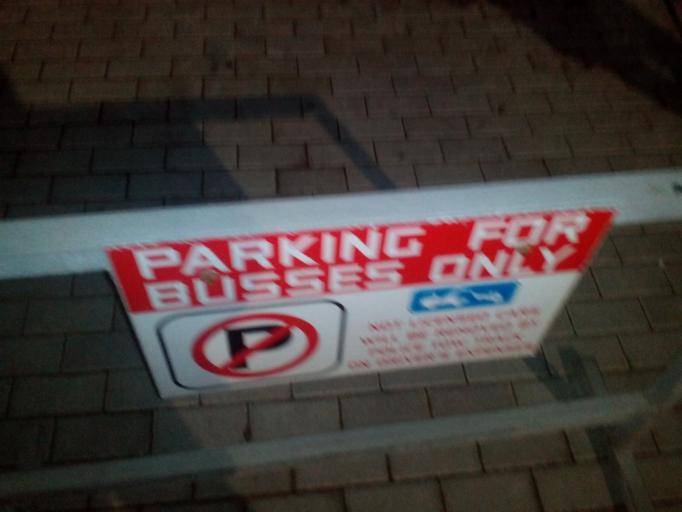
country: GR
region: Crete
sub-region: Nomos Rethymnis
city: Rethymno
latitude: 35.3682
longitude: 24.5061
